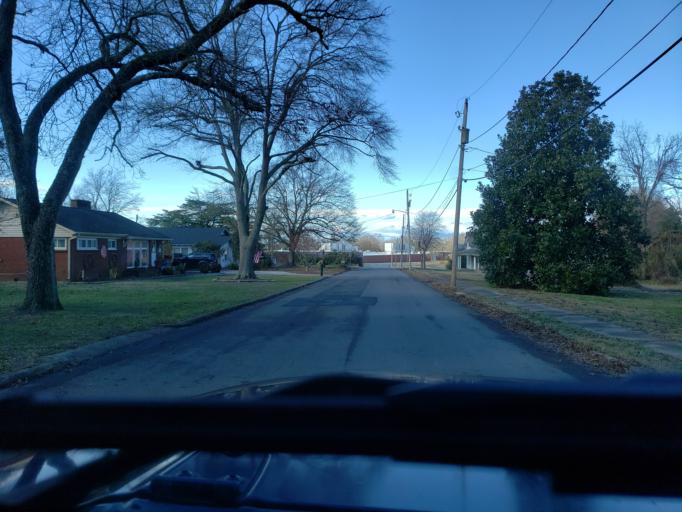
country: US
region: North Carolina
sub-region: Cleveland County
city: White Plains
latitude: 35.1702
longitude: -81.4497
